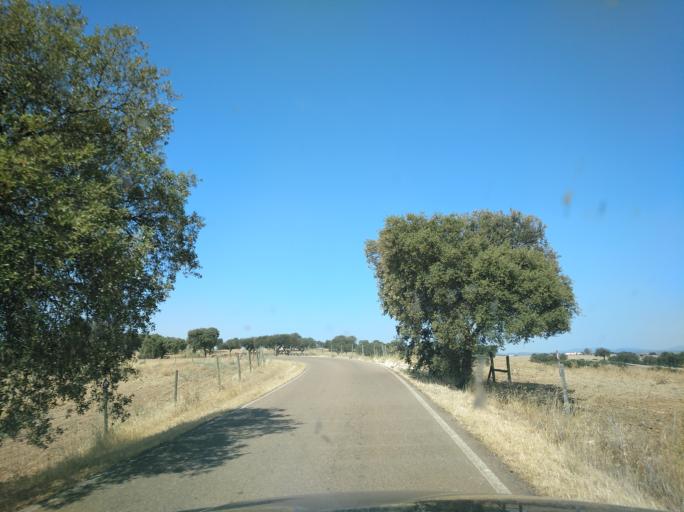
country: PT
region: Portalegre
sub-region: Campo Maior
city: Campo Maior
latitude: 39.0476
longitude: -7.0112
